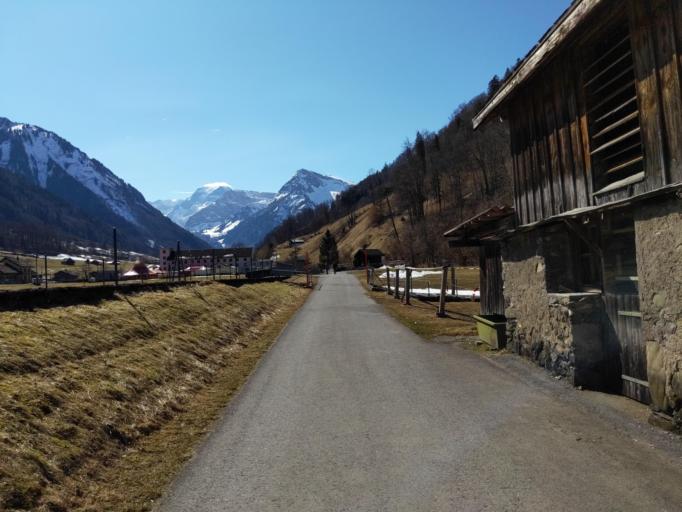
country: CH
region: Glarus
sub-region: Glarus
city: Luchsingen
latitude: 46.9484
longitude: 9.0250
